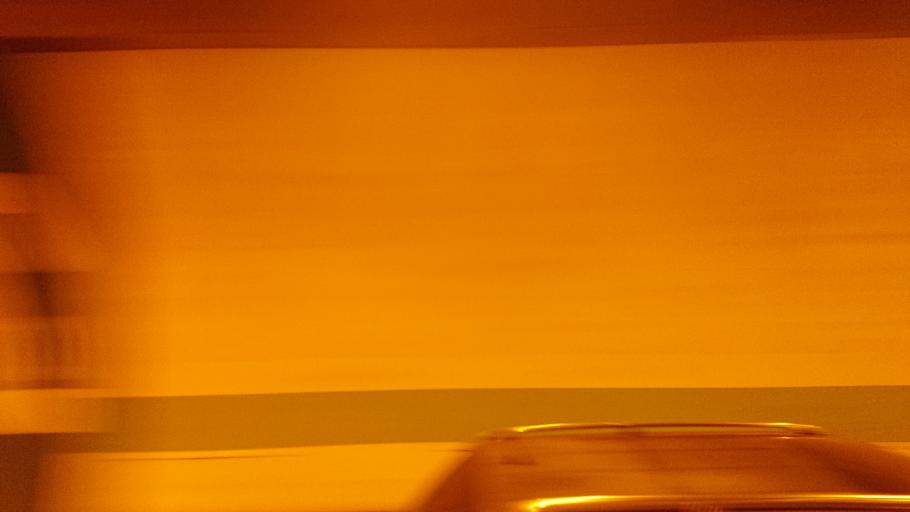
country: TW
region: Taiwan
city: Zhongxing New Village
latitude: 24.0037
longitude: 120.8189
